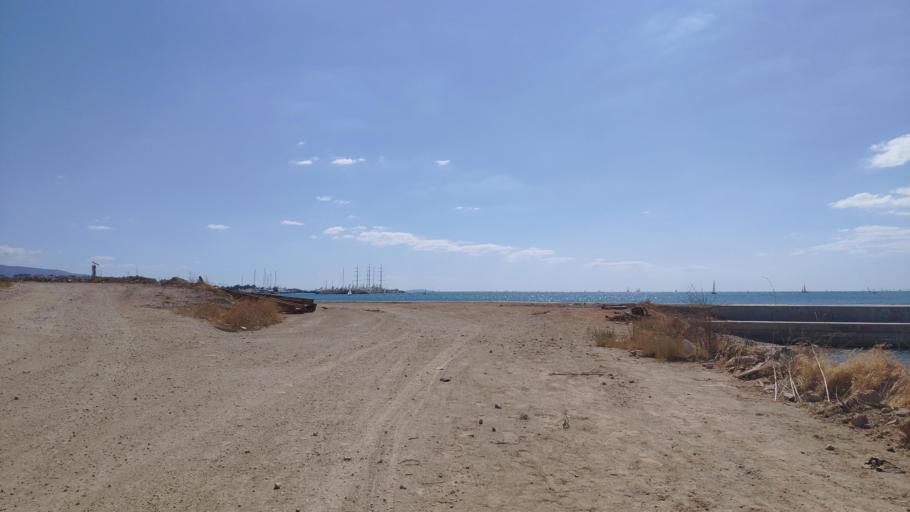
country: GR
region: Attica
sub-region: Nomarchia Athinas
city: Moskhaton
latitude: 37.9420
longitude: 23.6740
